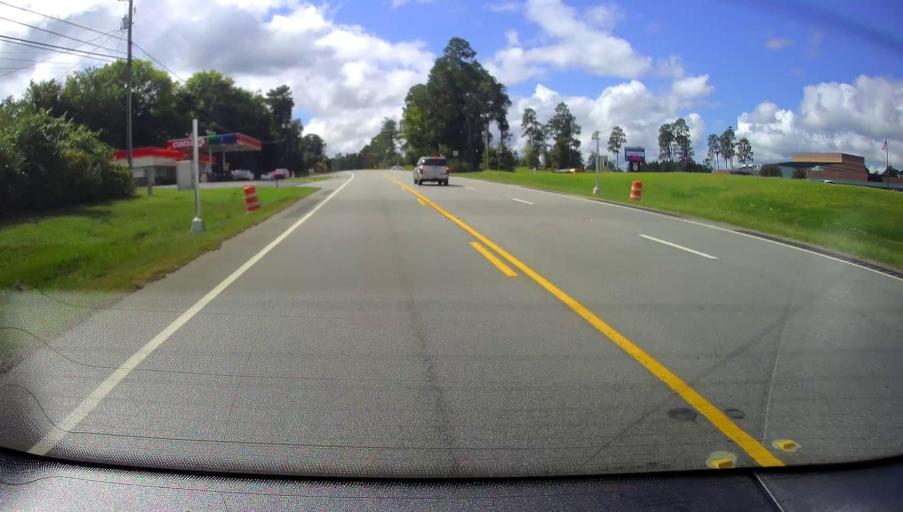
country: US
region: Georgia
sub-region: Baldwin County
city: Milledgeville
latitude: 33.0710
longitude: -83.2582
